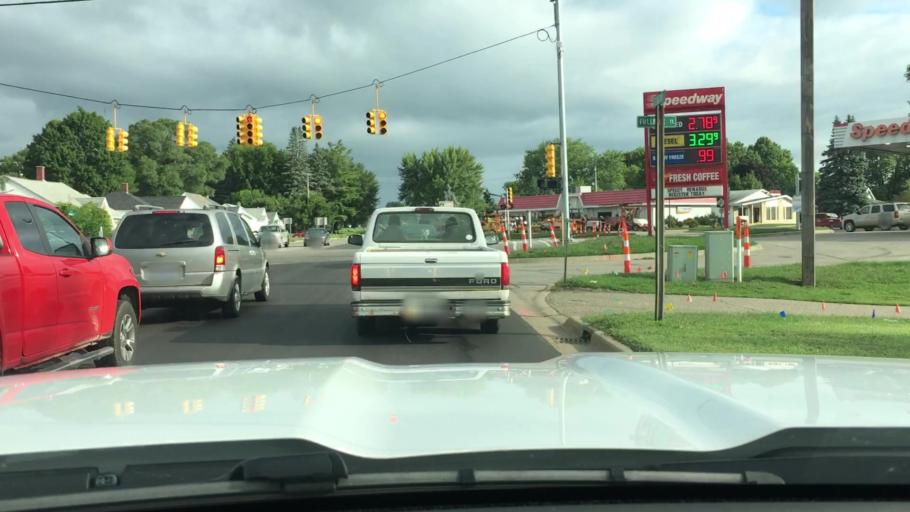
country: US
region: Michigan
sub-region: Tuscola County
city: Caro
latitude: 43.4954
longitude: -83.3874
